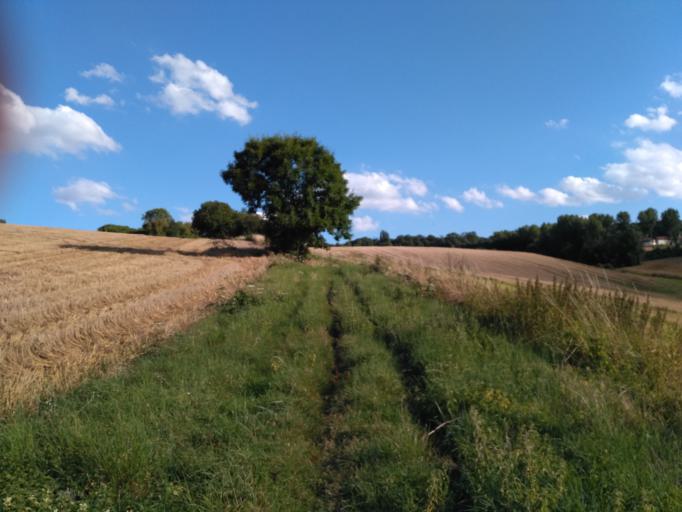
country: FR
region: Ile-de-France
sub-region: Departement du Val-d'Oise
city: Maffliers
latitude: 49.0962
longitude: 2.2803
